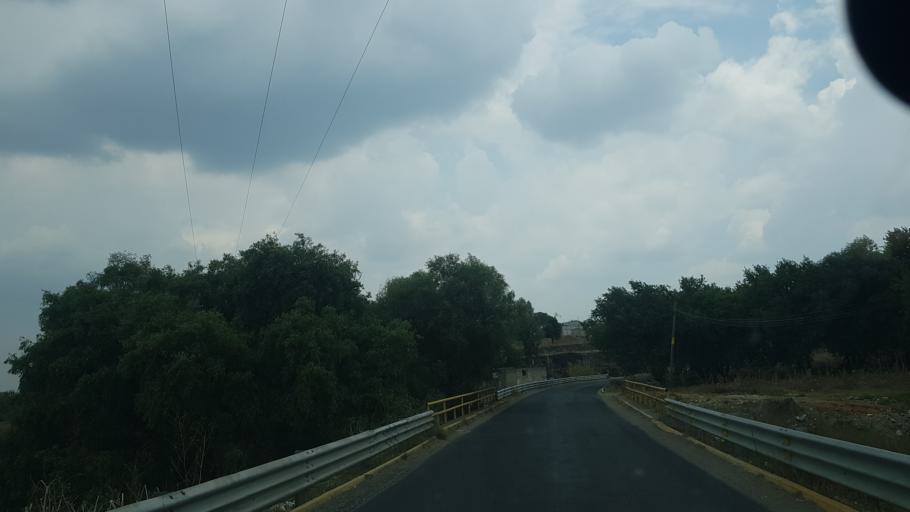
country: MX
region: Puebla
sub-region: Huejotzingo
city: San Miguel Tianguizolco
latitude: 19.1601
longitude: -98.4332
